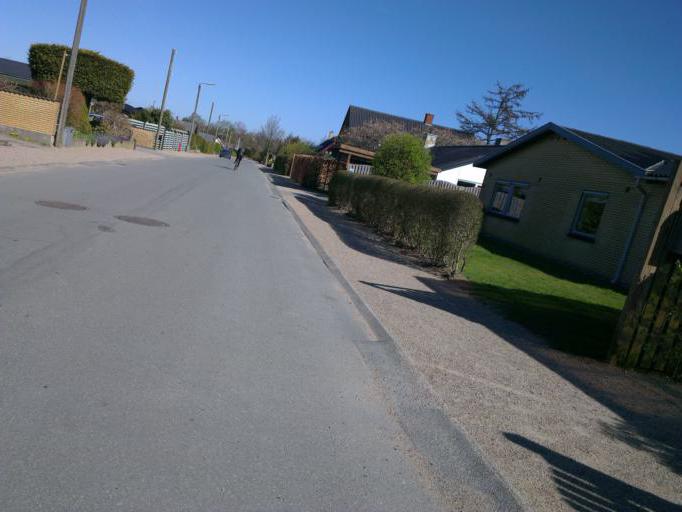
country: DK
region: Capital Region
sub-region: Frederikssund Kommune
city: Frederikssund
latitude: 55.8245
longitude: 12.0811
